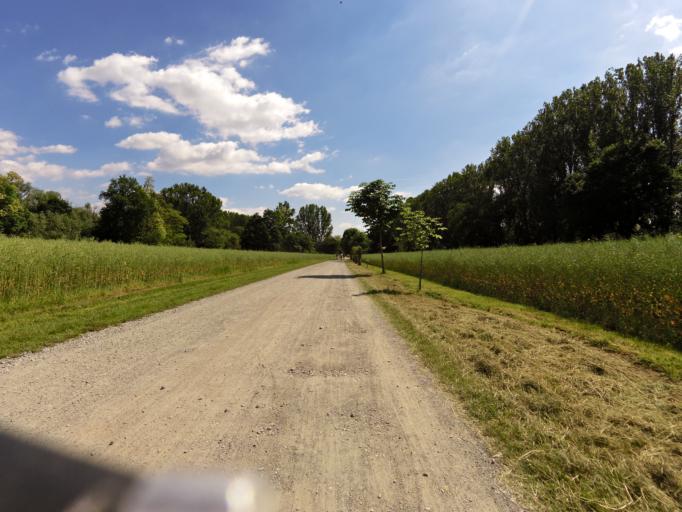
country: DE
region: Rheinland-Pfalz
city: Nackenheim
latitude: 49.9370
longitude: 8.3503
